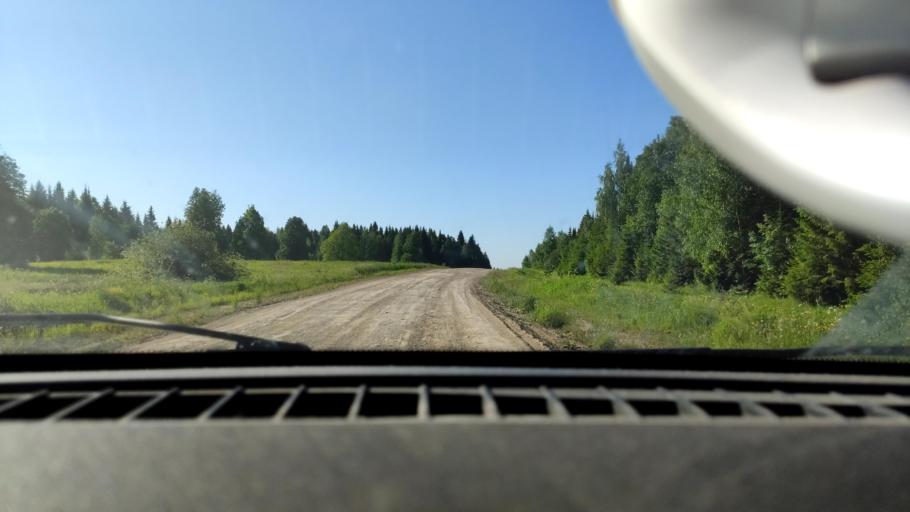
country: RU
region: Perm
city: Novyye Lyady
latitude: 58.1808
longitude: 56.5884
